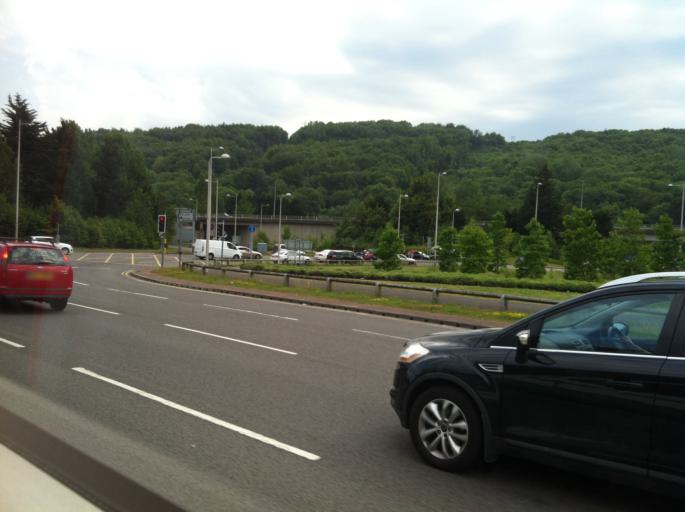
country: GB
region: Wales
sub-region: Cardiff
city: Cardiff
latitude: 51.4719
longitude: -3.2124
